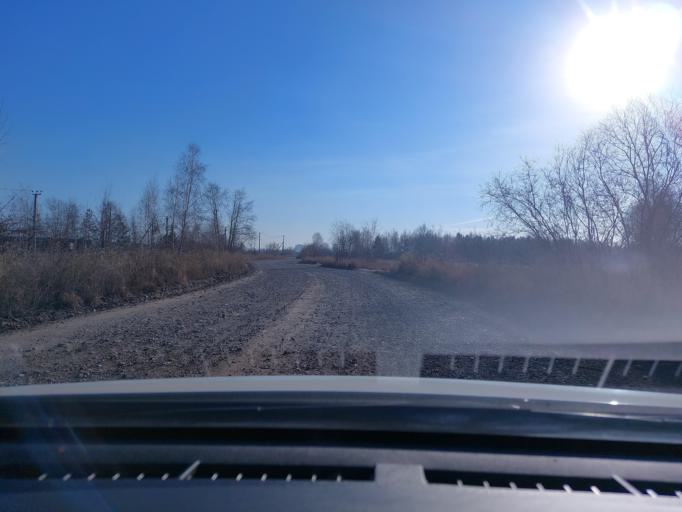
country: RU
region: Irkutsk
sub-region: Irkutskiy Rayon
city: Irkutsk
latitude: 52.3071
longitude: 104.2730
